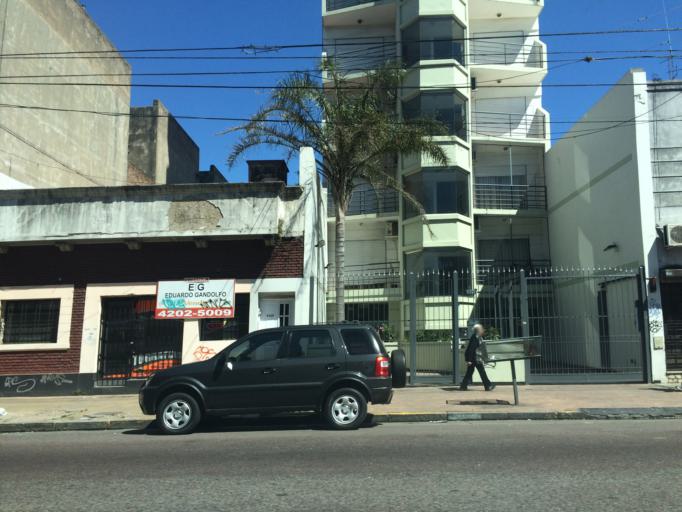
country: AR
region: Buenos Aires
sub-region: Partido de Lanus
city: Lanus
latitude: -34.7289
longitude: -58.3961
